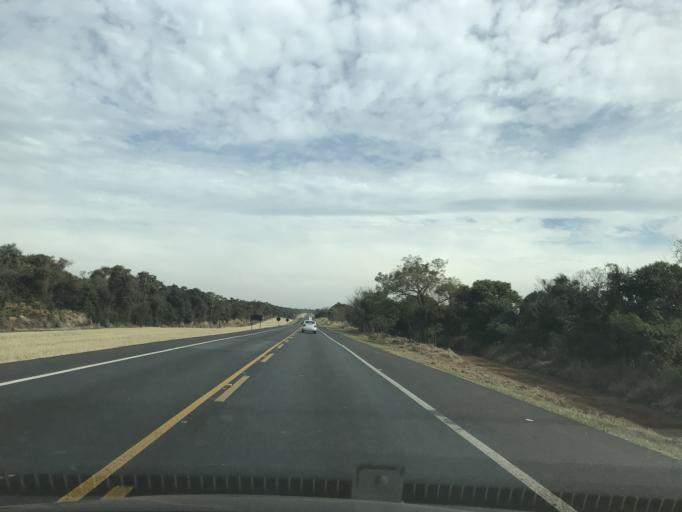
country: BR
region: Parana
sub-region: Cascavel
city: Cascavel
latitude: -25.0565
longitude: -53.6408
